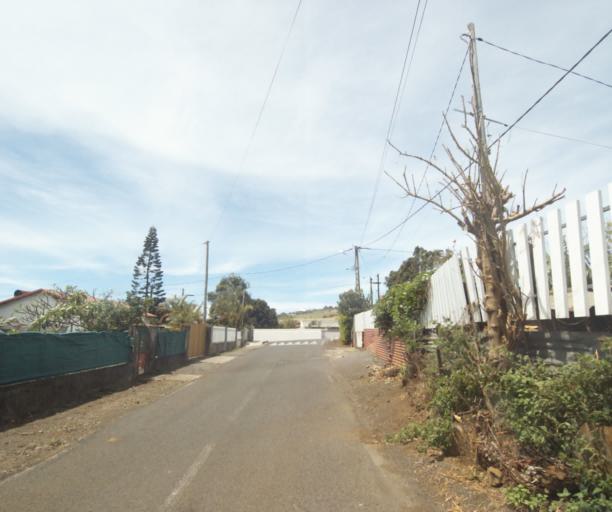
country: RE
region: Reunion
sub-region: Reunion
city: Saint-Paul
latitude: -21.0441
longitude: 55.2832
